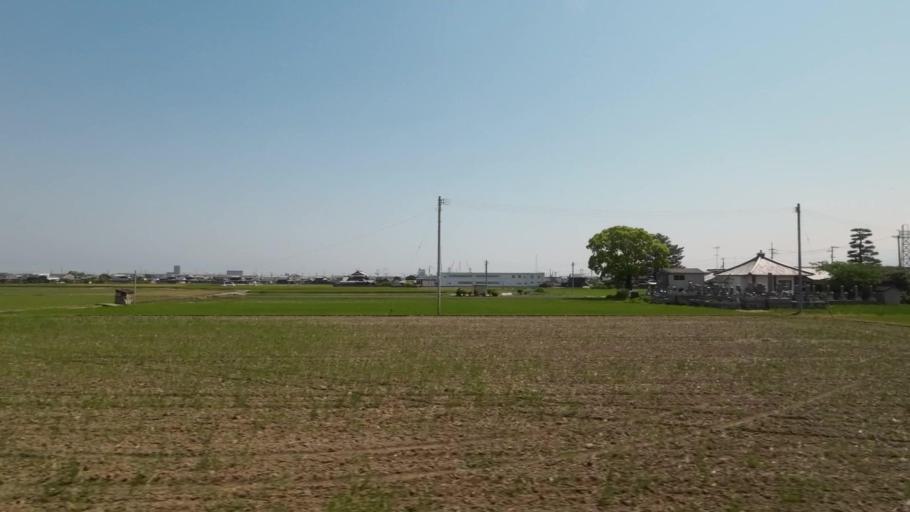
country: JP
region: Ehime
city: Saijo
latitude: 33.9205
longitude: 133.0937
